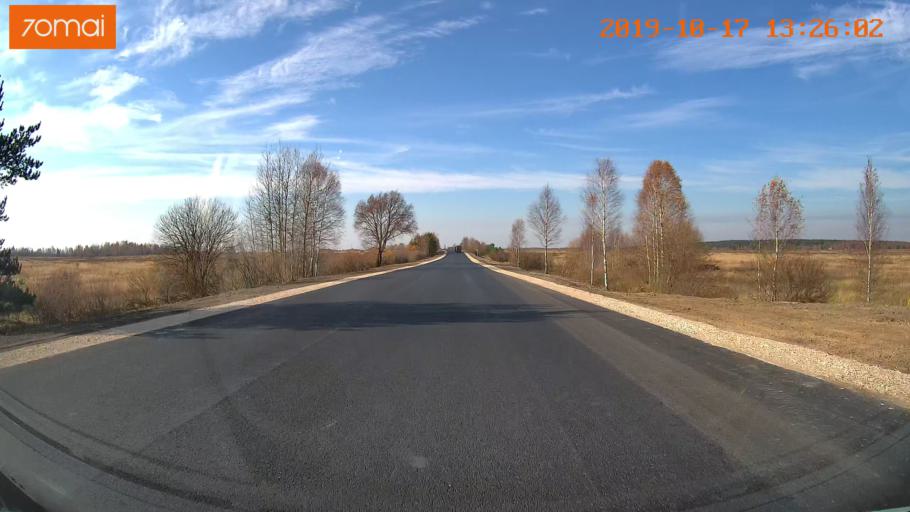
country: RU
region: Rjazan
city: Gus'-Zheleznyy
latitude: 55.1072
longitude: 40.9310
